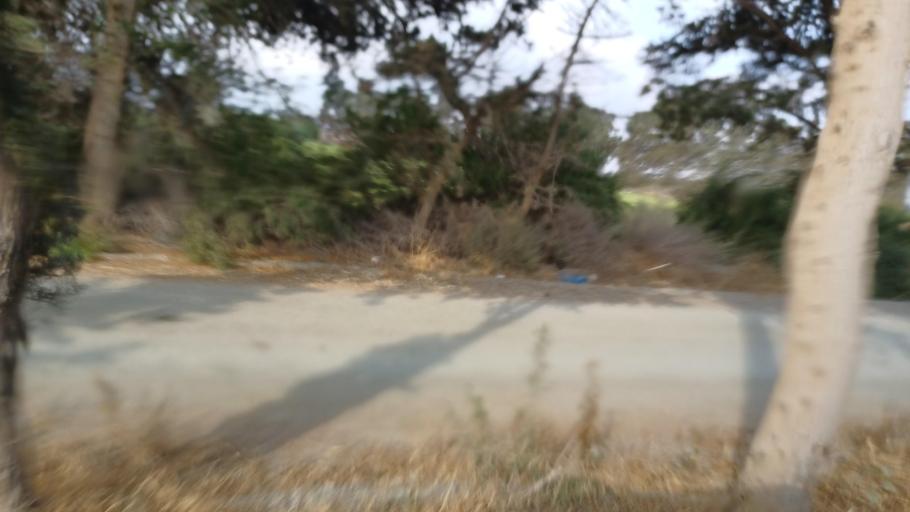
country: CY
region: Larnaka
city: Meneou
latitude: 34.8467
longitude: 33.5951
